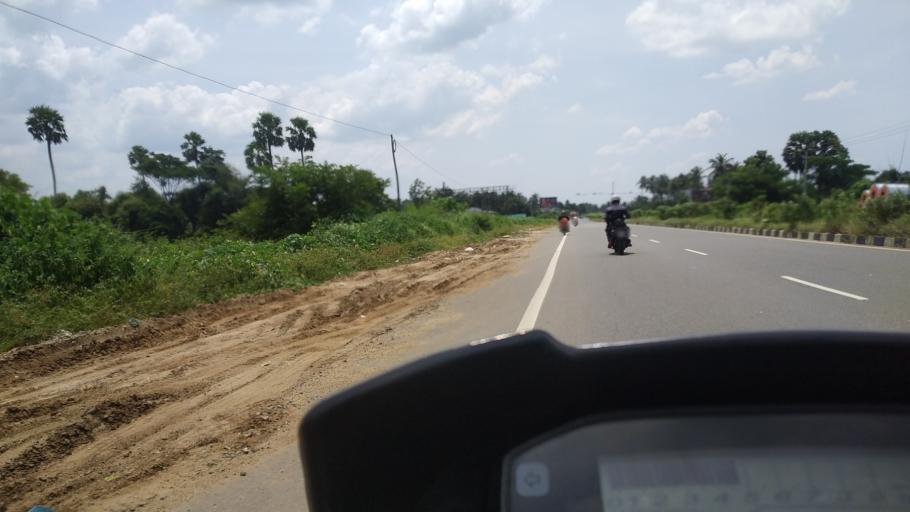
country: IN
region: Kerala
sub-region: Palakkad district
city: Chittur
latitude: 10.8054
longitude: 76.7889
